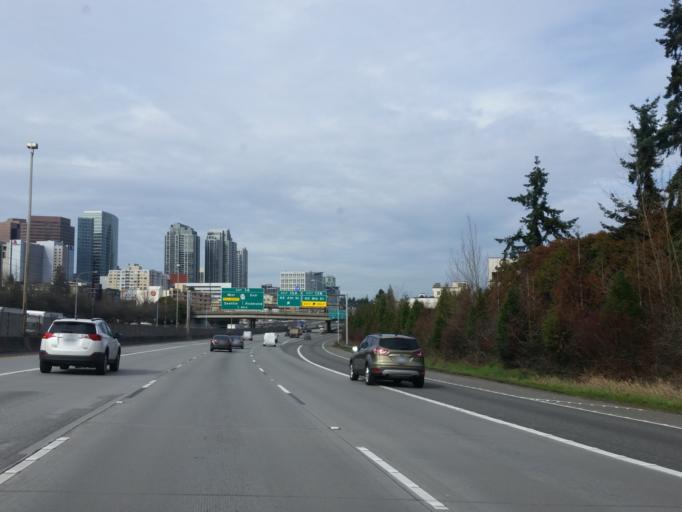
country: US
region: Washington
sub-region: King County
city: Bellevue
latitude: 47.6073
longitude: -122.1873
